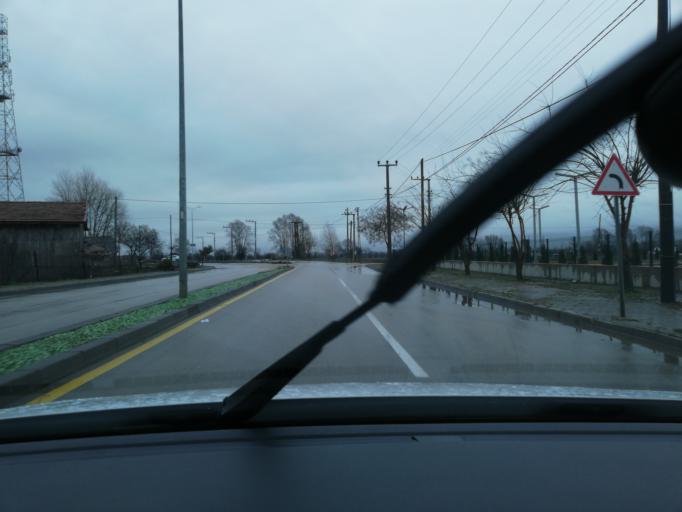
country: TR
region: Bolu
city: Bolu
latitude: 40.7232
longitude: 31.6168
